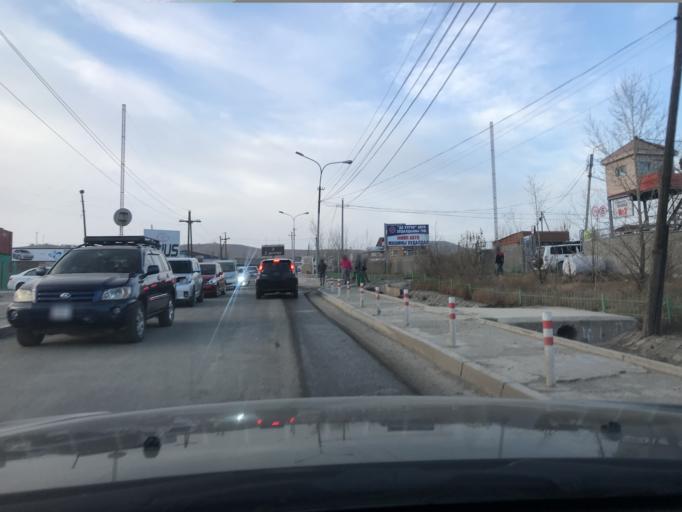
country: MN
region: Ulaanbaatar
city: Ulaanbaatar
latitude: 47.9286
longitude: 106.9978
